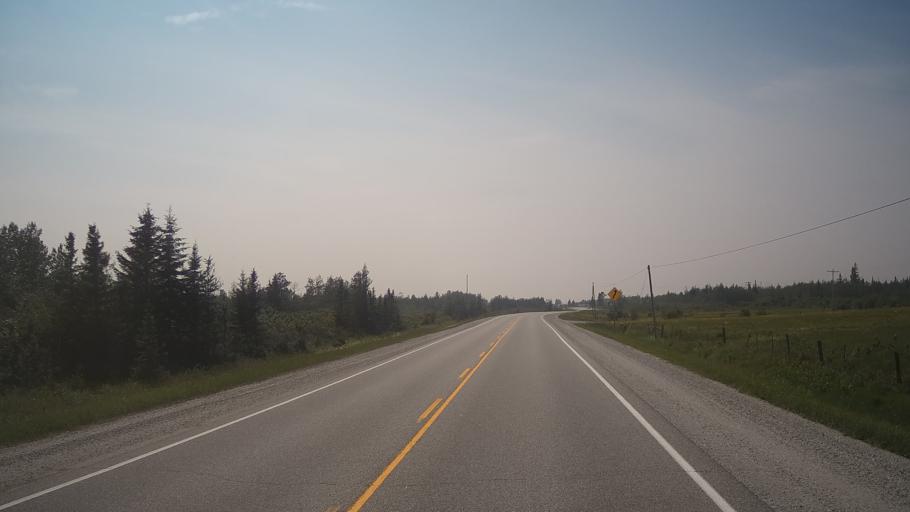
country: CA
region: Ontario
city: Kapuskasing
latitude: 49.2876
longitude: -81.8452
